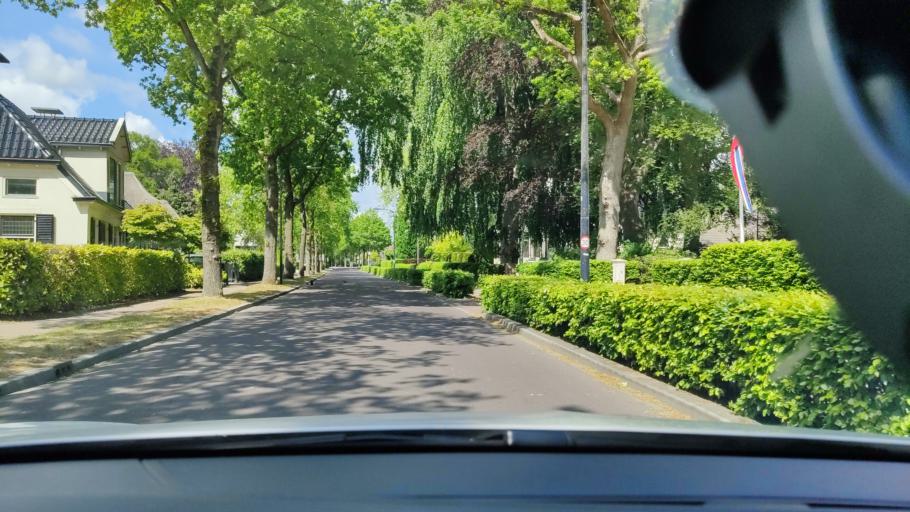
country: NL
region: Drenthe
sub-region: Gemeente Tynaarlo
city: Zuidlaren
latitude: 53.0976
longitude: 6.6890
